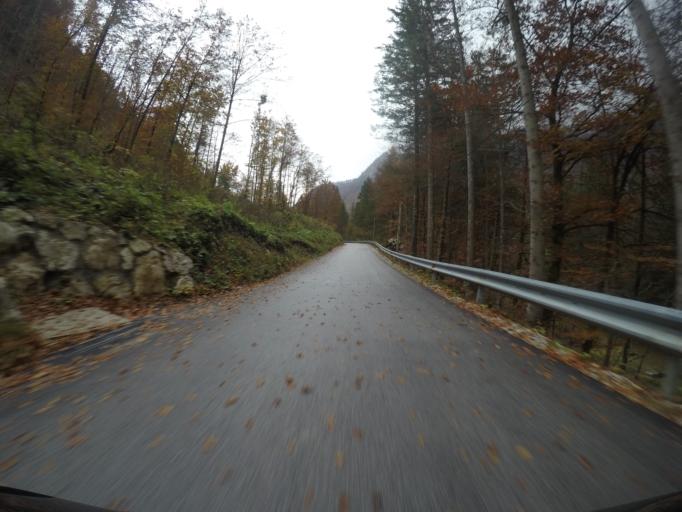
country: SI
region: Jesenice
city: Hrusica
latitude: 46.3976
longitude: 14.0017
